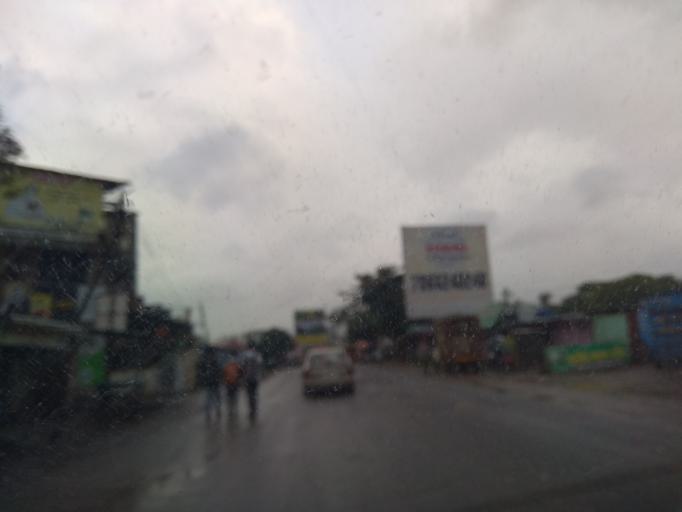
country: IN
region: Maharashtra
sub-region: Pune Division
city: Kharakvasla
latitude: 18.5107
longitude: 73.6886
